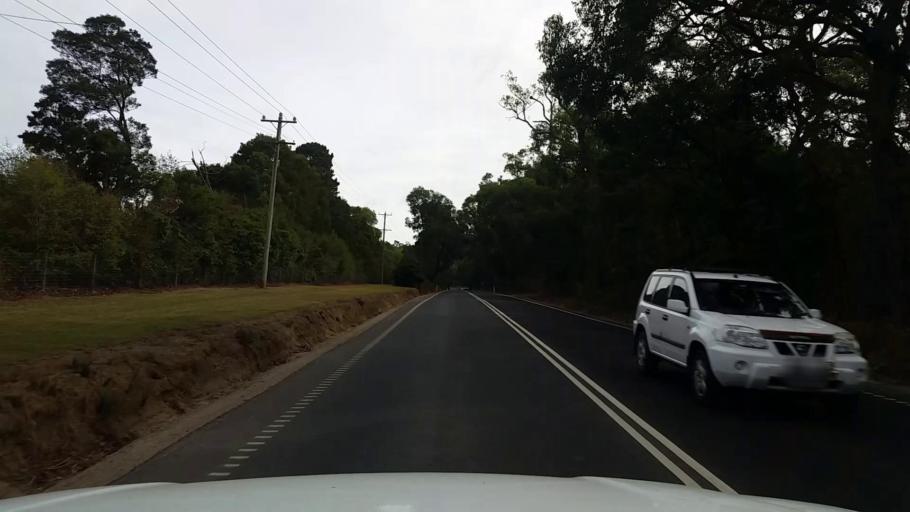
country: AU
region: Victoria
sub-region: Mornington Peninsula
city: Balnarring
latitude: -38.3439
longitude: 145.1006
